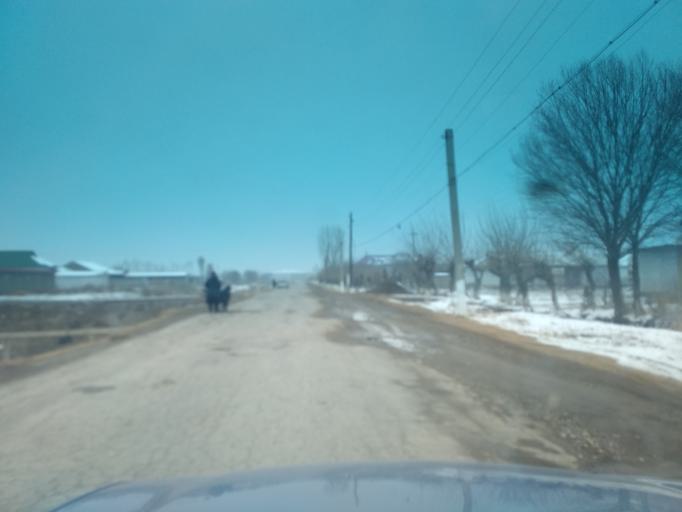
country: UZ
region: Sirdaryo
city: Guliston
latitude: 40.4809
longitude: 68.7512
